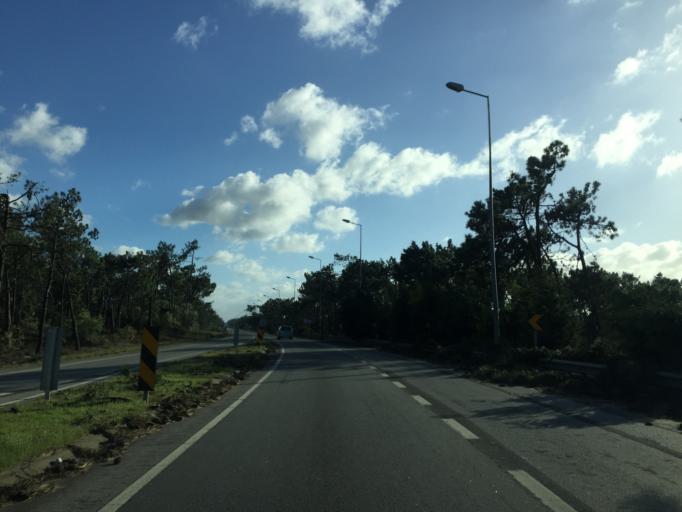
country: PT
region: Coimbra
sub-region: Figueira da Foz
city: Figueira da Foz
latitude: 40.1182
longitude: -8.8561
